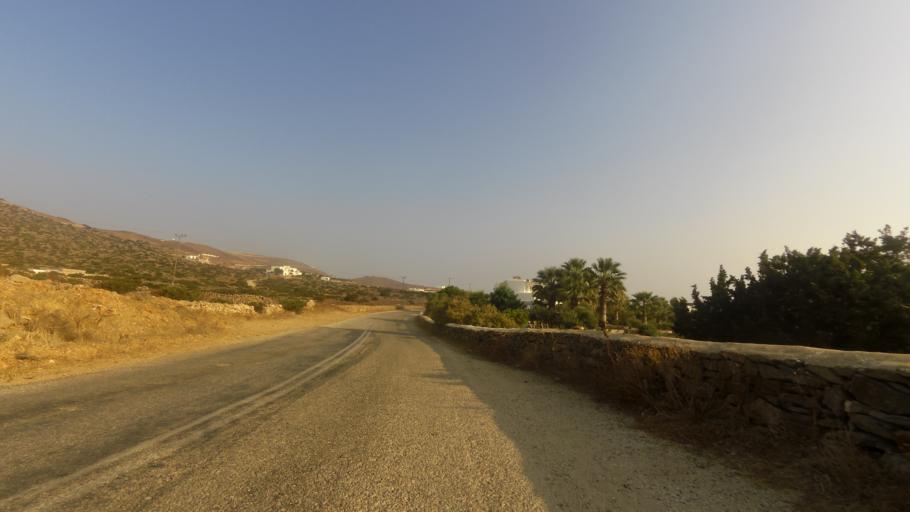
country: GR
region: South Aegean
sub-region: Nomos Kykladon
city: Antiparos
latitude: 37.0232
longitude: 25.0769
